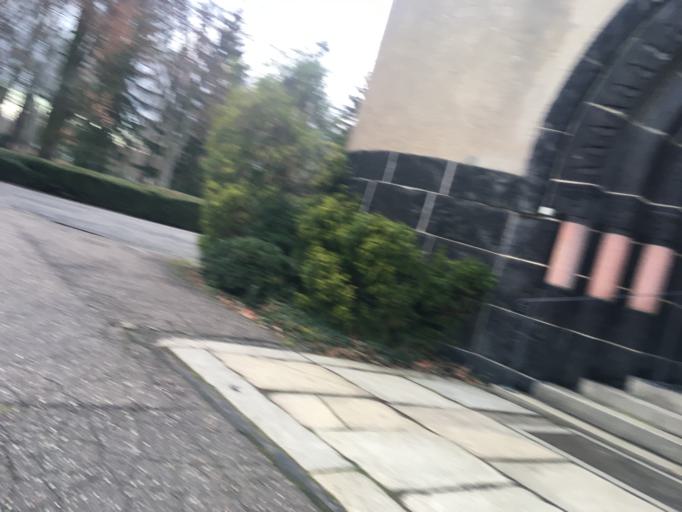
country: DE
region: Berlin
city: Reinickendorf
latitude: 52.5683
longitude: 13.3317
